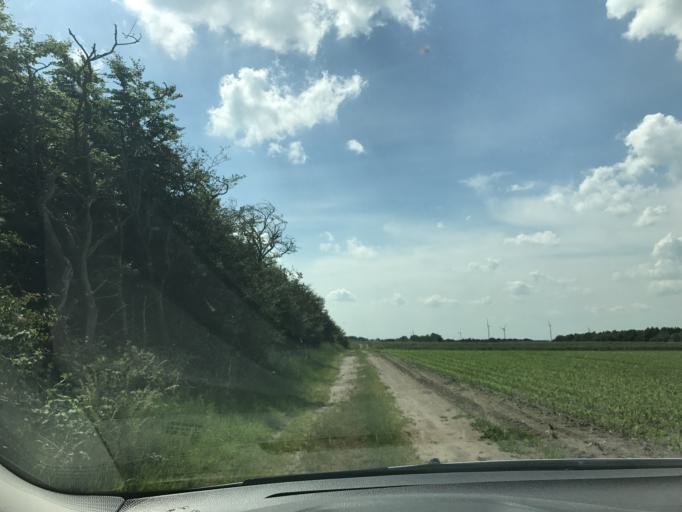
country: DE
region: Schleswig-Holstein
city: Ellhoft
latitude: 54.9262
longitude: 8.9520
